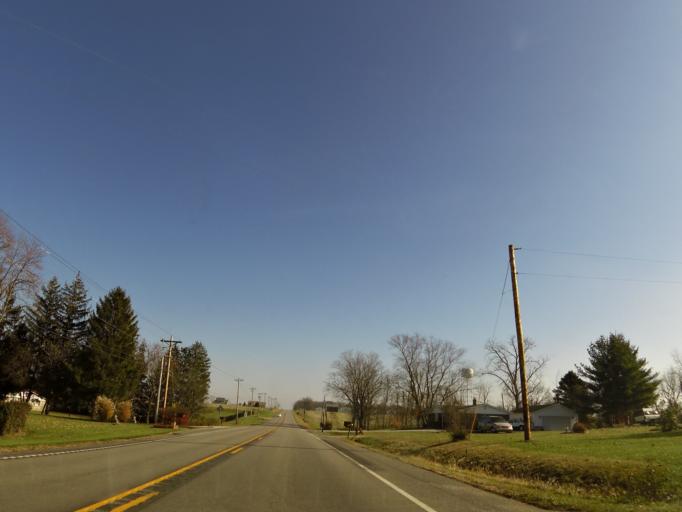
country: US
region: Indiana
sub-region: Union County
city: Liberty
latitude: 39.6402
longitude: -84.9762
